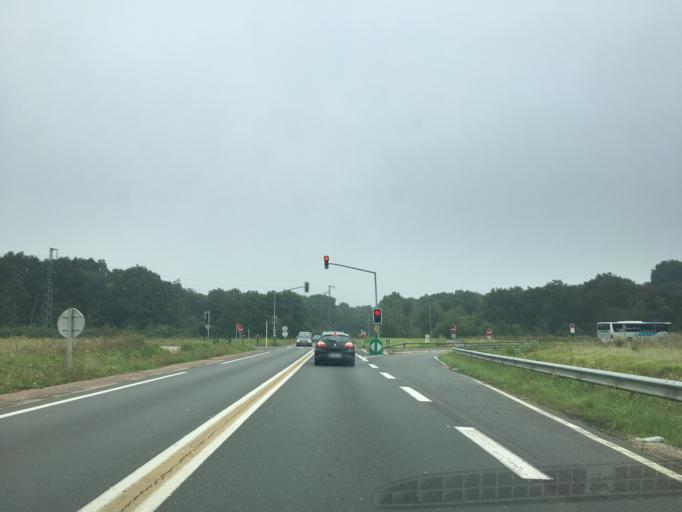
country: FR
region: Ile-de-France
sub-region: Departement de l'Essonne
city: Tigery
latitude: 48.6558
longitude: 2.5109
